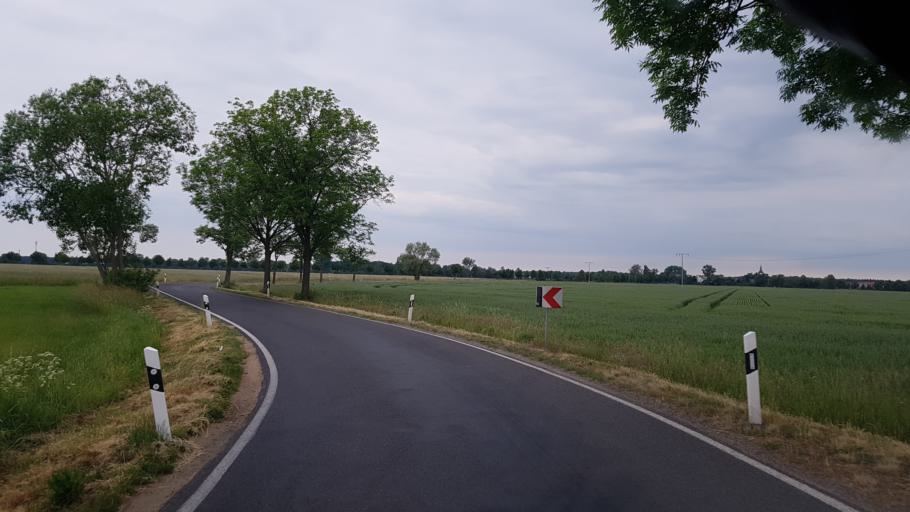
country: DE
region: Saxony-Anhalt
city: Holzdorf
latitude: 51.8041
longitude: 13.2338
